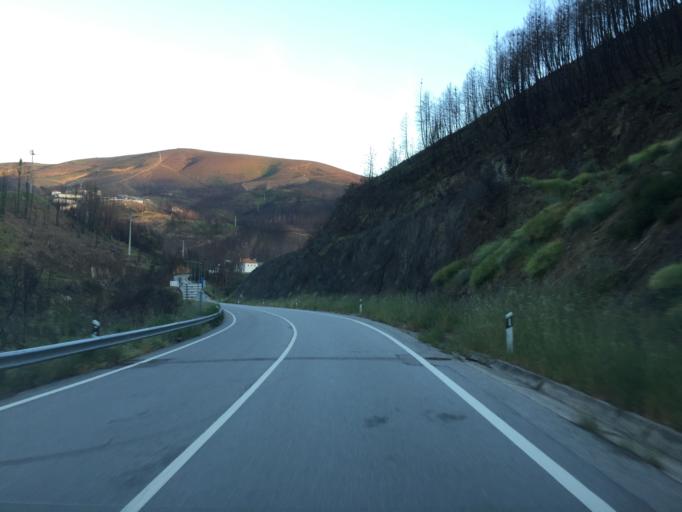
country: PT
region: Coimbra
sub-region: Pampilhosa da Serra
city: Pampilhosa da Serra
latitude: 40.0513
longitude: -7.9617
